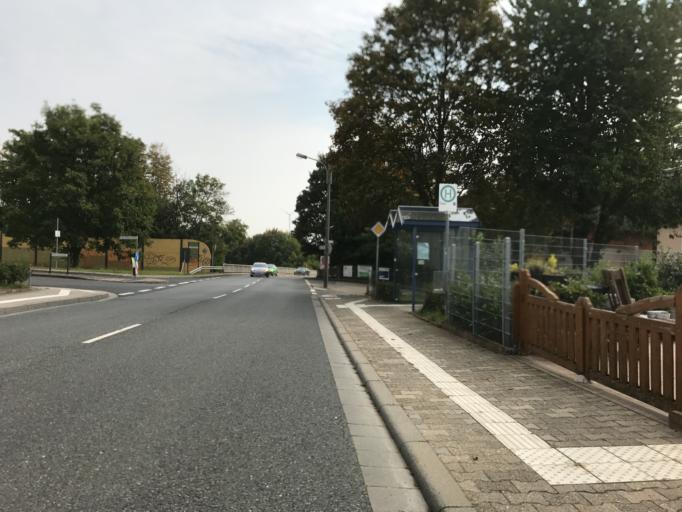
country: DE
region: Rheinland-Pfalz
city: Klein-Winternheim
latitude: 49.9383
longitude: 8.2018
